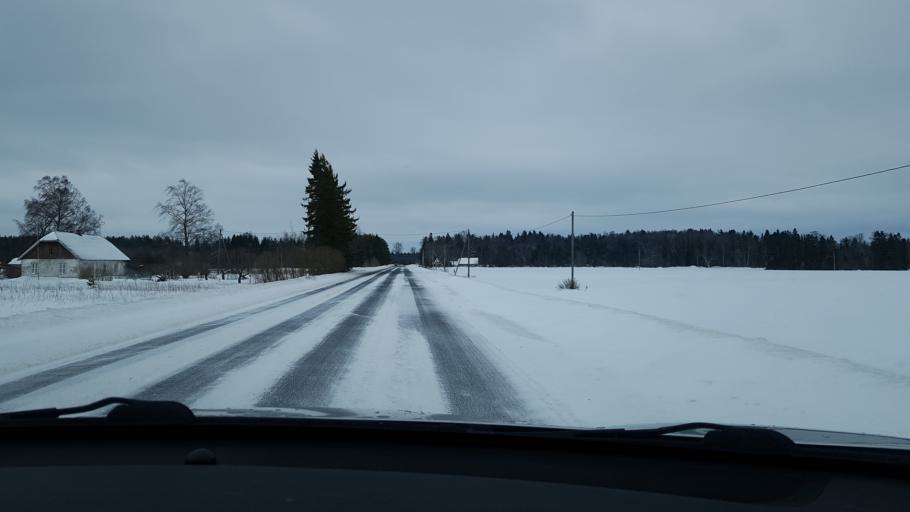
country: EE
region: Jaervamaa
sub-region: Jaerva-Jaani vald
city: Jarva-Jaani
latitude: 59.1078
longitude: 25.8034
